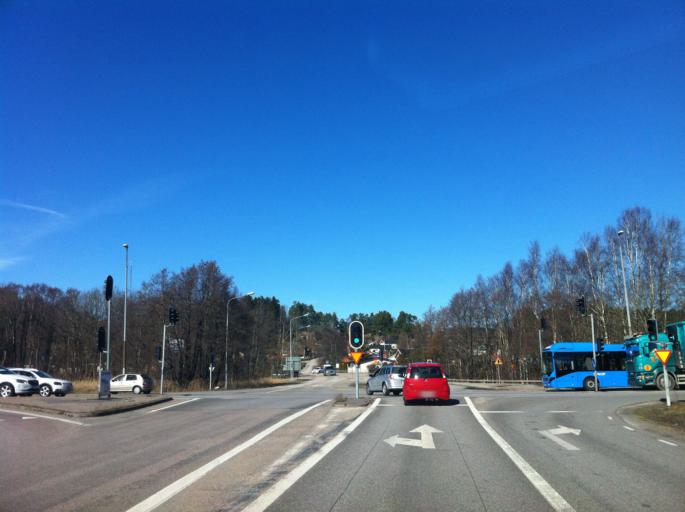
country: SE
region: Vaestra Goetaland
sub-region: Uddevalla Kommun
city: Uddevalla
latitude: 58.3518
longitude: 11.8503
